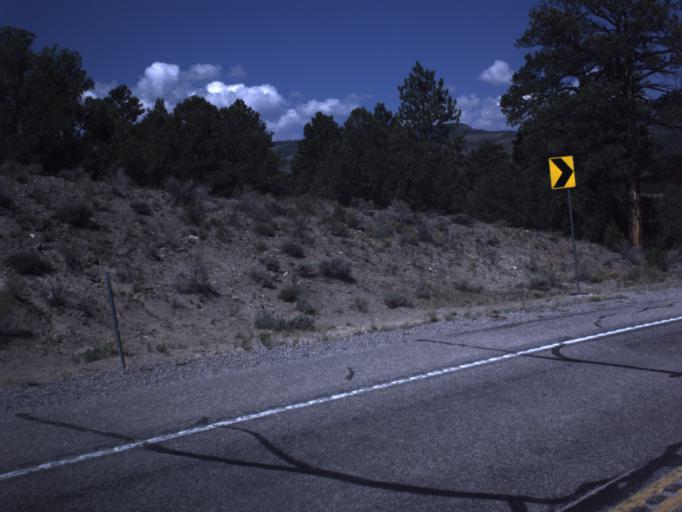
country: US
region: Utah
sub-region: Wayne County
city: Loa
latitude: 38.6464
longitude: -111.4435
